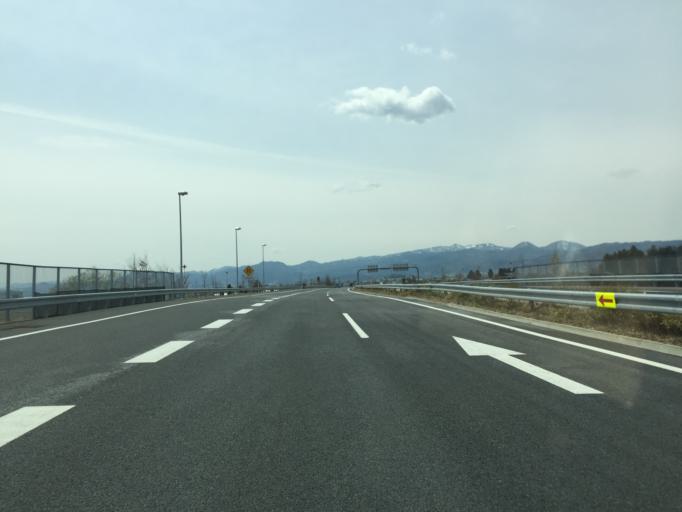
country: JP
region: Yamagata
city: Tendo
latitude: 38.3060
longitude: 140.3139
